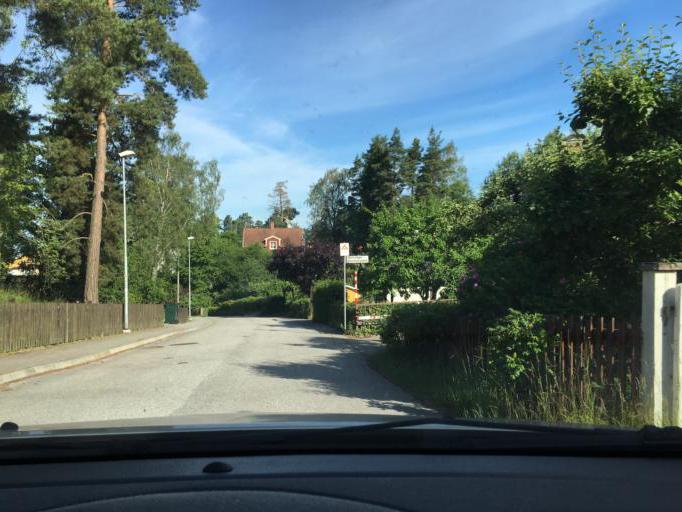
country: SE
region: Stockholm
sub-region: Sodertalje Kommun
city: Pershagen
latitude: 59.1846
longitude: 17.6586
